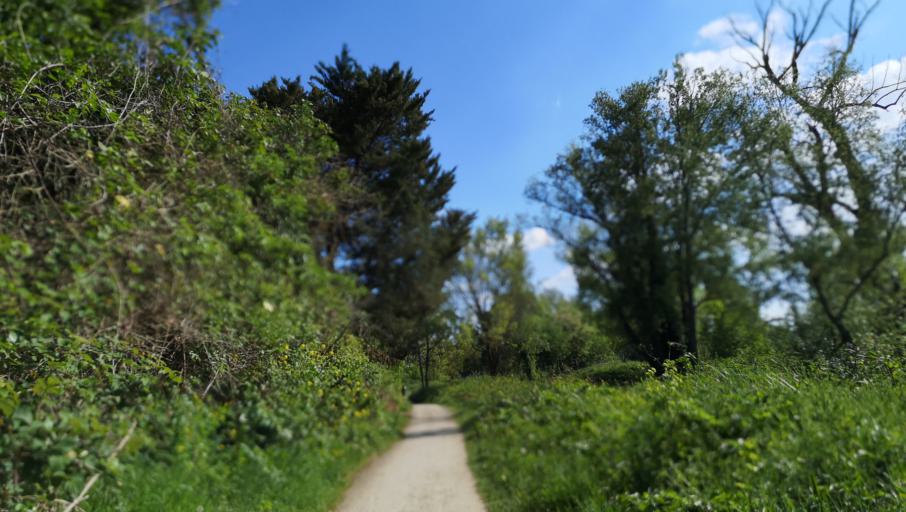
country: FR
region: Midi-Pyrenees
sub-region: Departement de la Haute-Garonne
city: Blagnac
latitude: 43.6349
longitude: 1.4049
